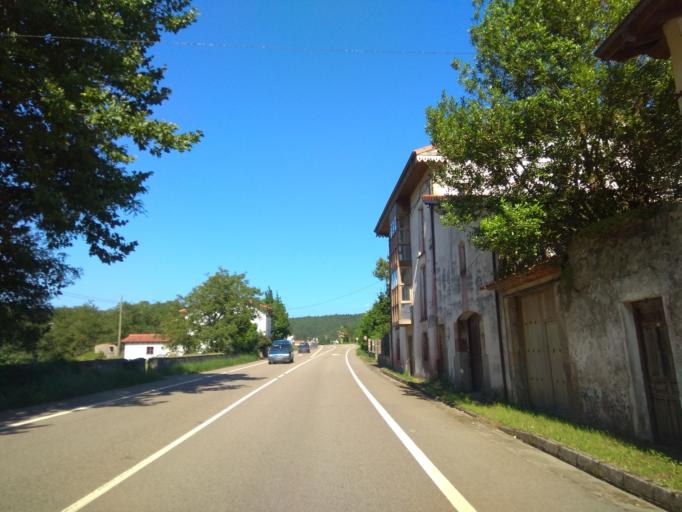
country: ES
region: Cantabria
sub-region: Provincia de Cantabria
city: Bareyo
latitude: 43.4673
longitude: -3.6657
